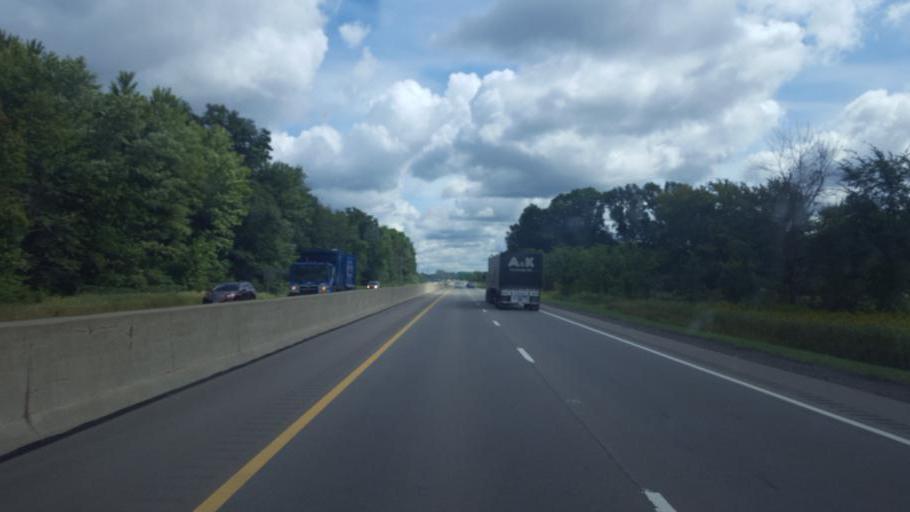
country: US
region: Ohio
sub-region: Lorain County
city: Elyria
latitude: 41.3263
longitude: -82.0851
